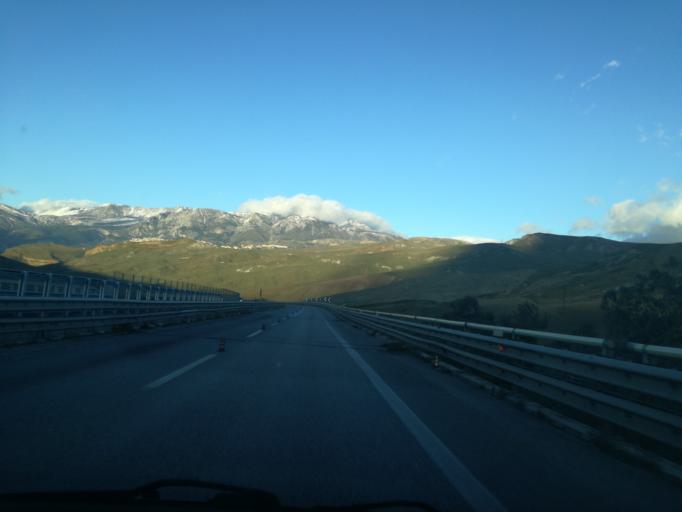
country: IT
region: Sicily
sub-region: Palermo
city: Polizzi Generosa
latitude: 37.7659
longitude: 13.9689
